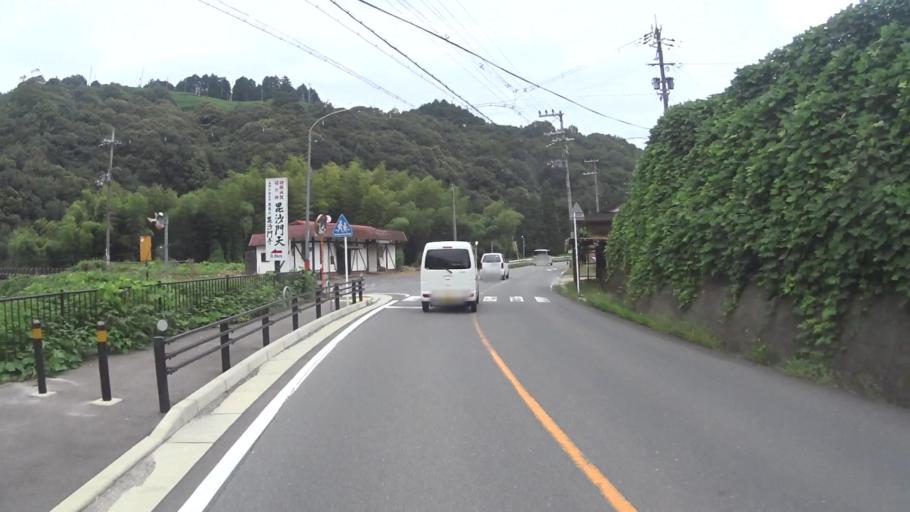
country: JP
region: Kyoto
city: Tanabe
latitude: 34.7890
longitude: 135.8865
